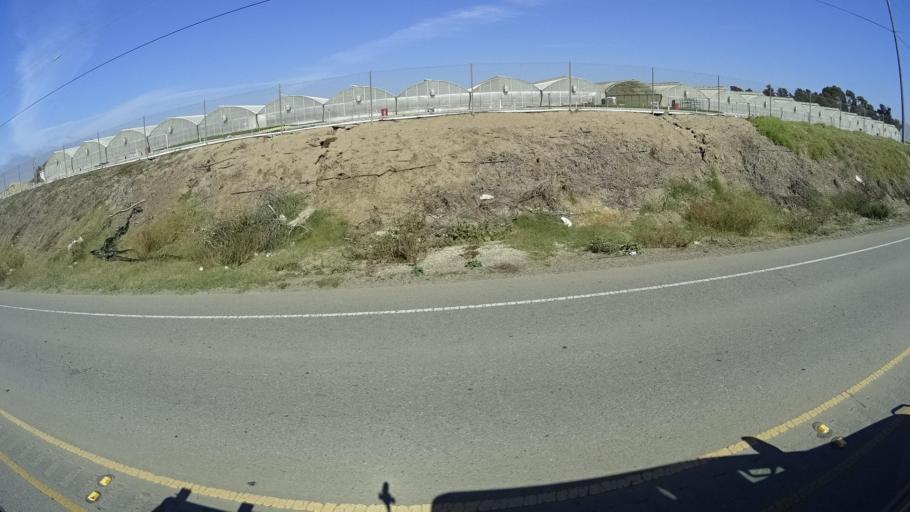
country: US
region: California
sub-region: Monterey County
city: Prunedale
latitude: 36.7455
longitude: -121.6935
